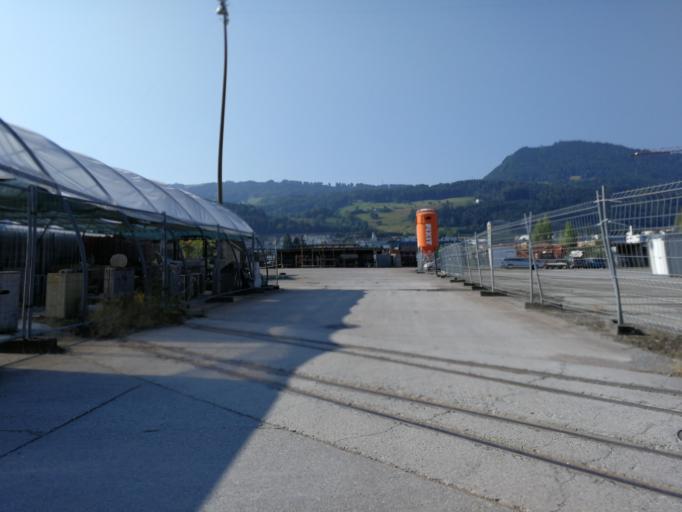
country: CH
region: Schwyz
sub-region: Bezirk Hoefe
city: Freienbach
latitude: 47.2065
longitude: 8.7783
